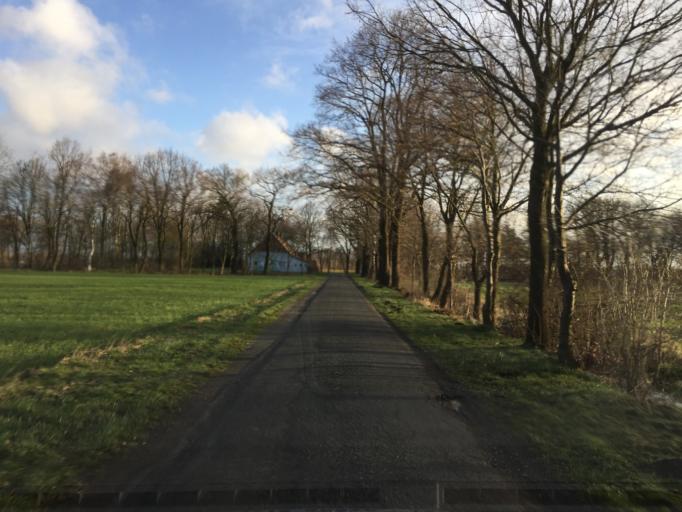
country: DE
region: Lower Saxony
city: Borstel
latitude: 52.6122
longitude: 8.9164
